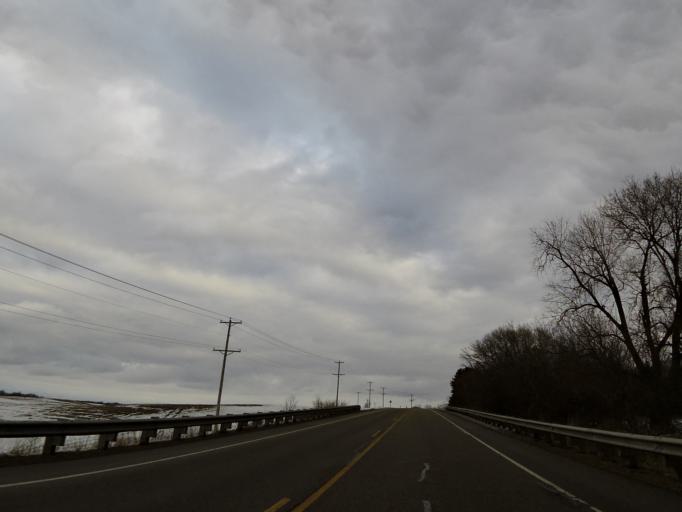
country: US
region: Minnesota
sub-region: Washington County
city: Bayport
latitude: 45.0427
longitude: -92.7641
